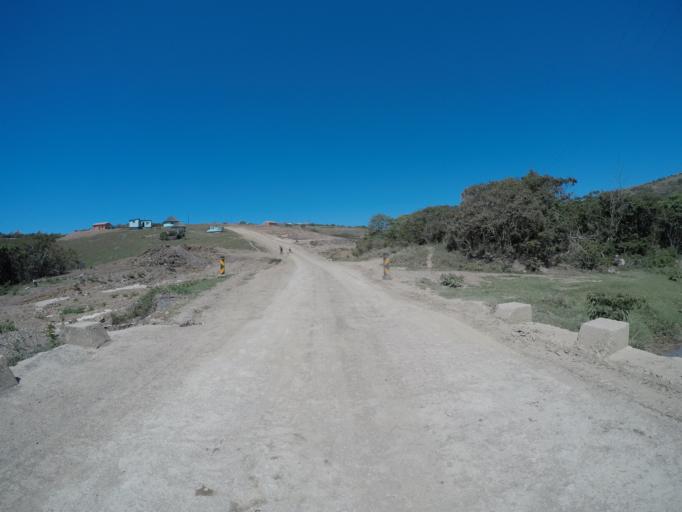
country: ZA
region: Eastern Cape
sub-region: OR Tambo District Municipality
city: Libode
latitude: -32.0183
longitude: 29.1155
